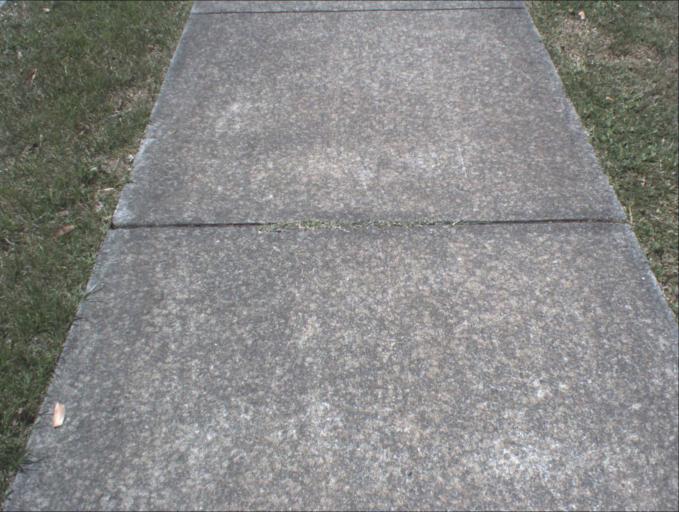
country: AU
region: Queensland
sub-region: Logan
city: Beenleigh
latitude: -27.6930
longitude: 153.2149
